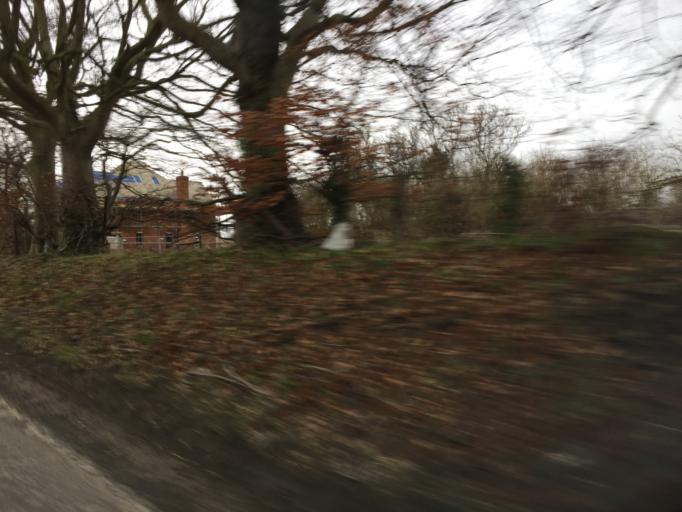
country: GB
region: England
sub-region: Oxfordshire
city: Harwell
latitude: 51.5979
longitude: -1.3008
